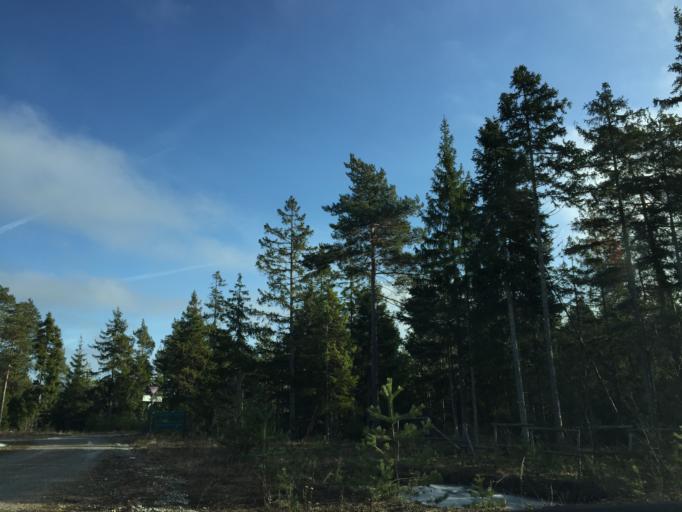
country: EE
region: Saare
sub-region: Kuressaare linn
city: Kuressaare
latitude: 58.4809
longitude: 21.9471
